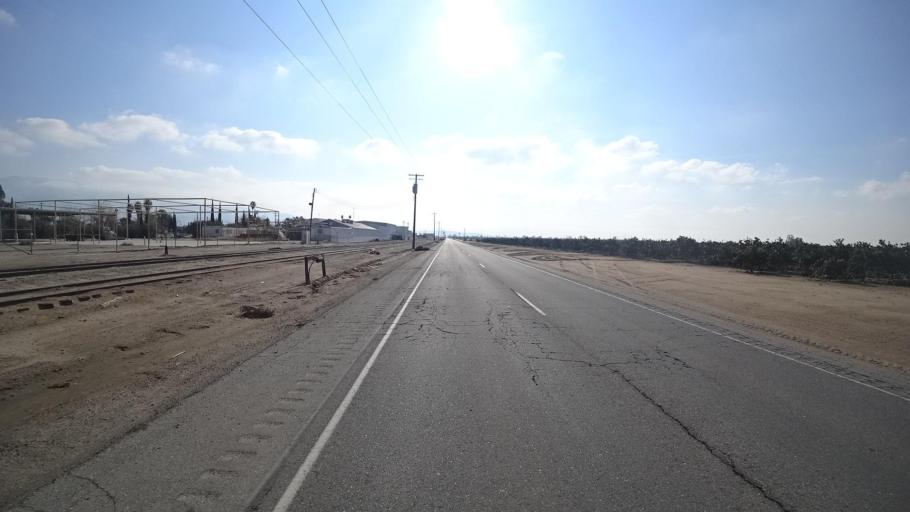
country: US
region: California
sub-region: Kern County
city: Arvin
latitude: 35.2292
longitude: -118.8244
